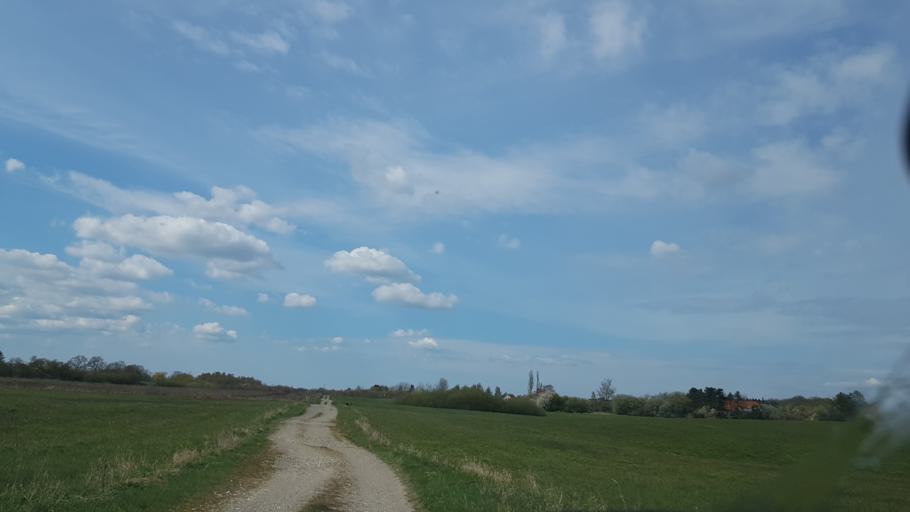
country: DK
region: Capital Region
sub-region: Allerod Kommune
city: Lillerod
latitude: 55.8955
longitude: 12.3374
